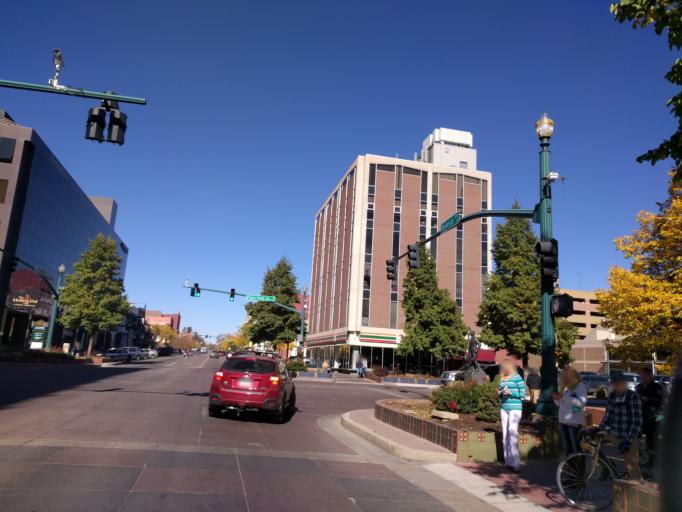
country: US
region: Colorado
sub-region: El Paso County
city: Colorado Springs
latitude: 38.8337
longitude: -104.8235
